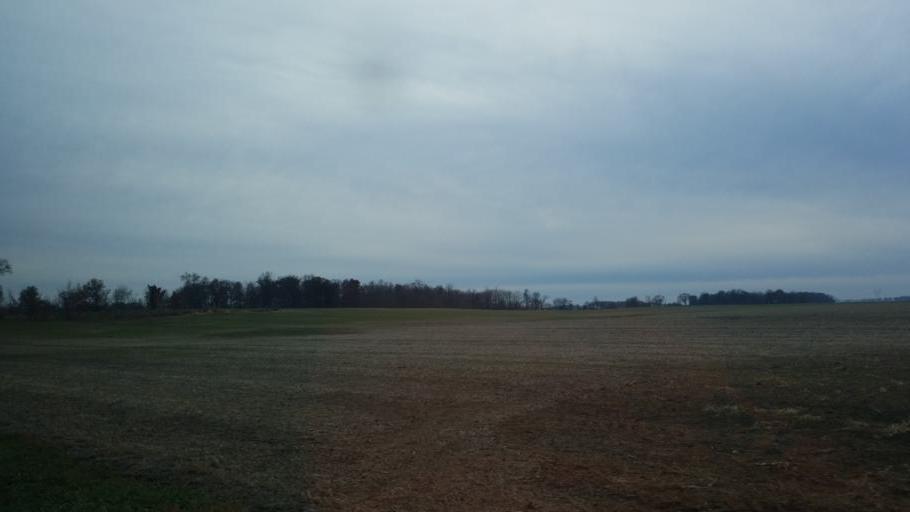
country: US
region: Indiana
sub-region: Adams County
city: Berne
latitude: 40.6695
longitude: -84.8595
